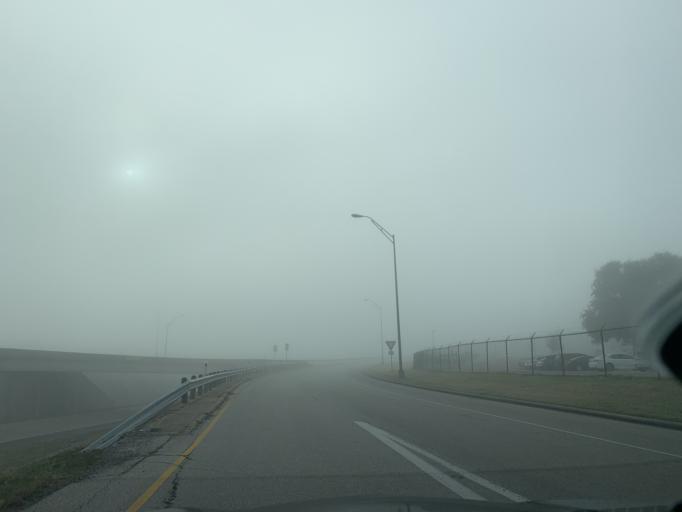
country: US
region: Texas
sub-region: Tarrant County
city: Euless
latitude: 32.8354
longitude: -97.0626
